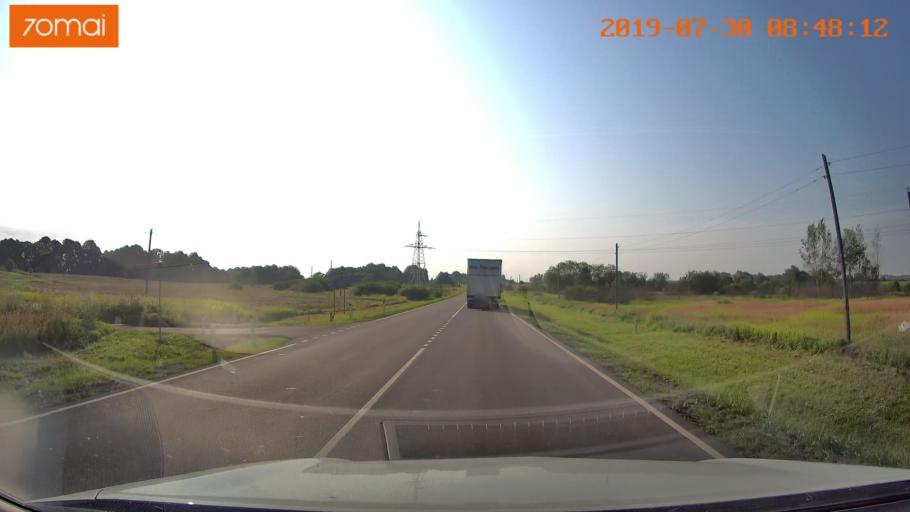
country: RU
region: Kaliningrad
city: Chernyakhovsk
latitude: 54.6191
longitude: 21.9020
